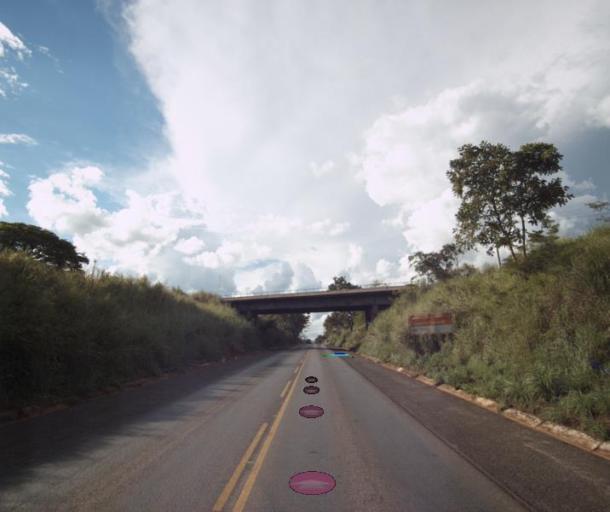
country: BR
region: Goias
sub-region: Rialma
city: Rialma
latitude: -15.3205
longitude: -49.5720
